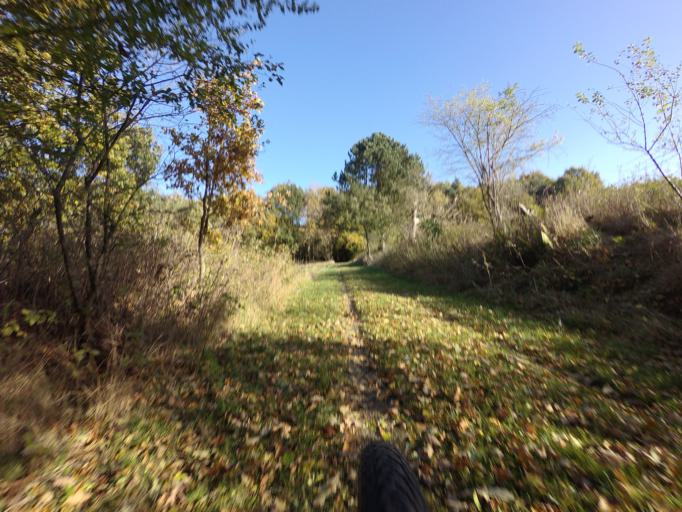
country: DK
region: Central Jutland
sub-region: Norddjurs Kommune
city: Grenaa
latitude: 56.4957
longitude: 10.7241
